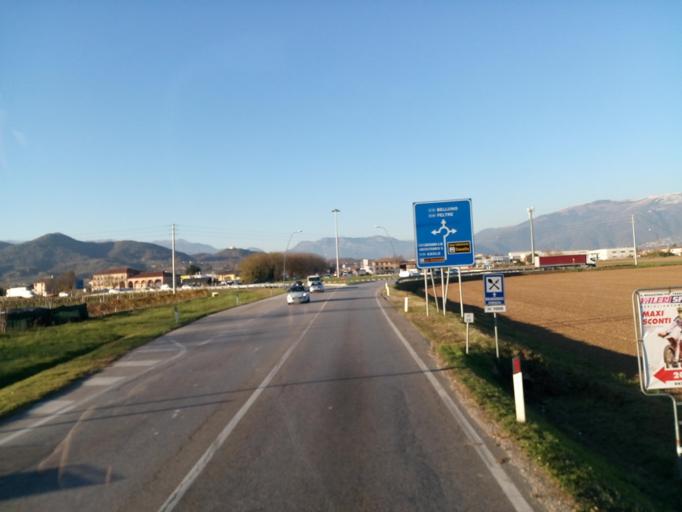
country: IT
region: Veneto
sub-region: Provincia di Treviso
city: Crocetta-Nogare
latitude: 45.8125
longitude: 12.0169
